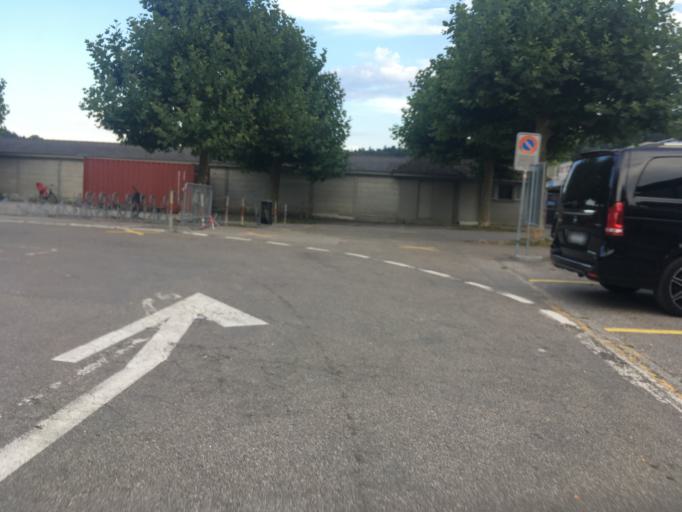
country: CH
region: Solothurn
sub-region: Bezirk Solothurn
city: Solothurn
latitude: 47.1992
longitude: 7.5261
